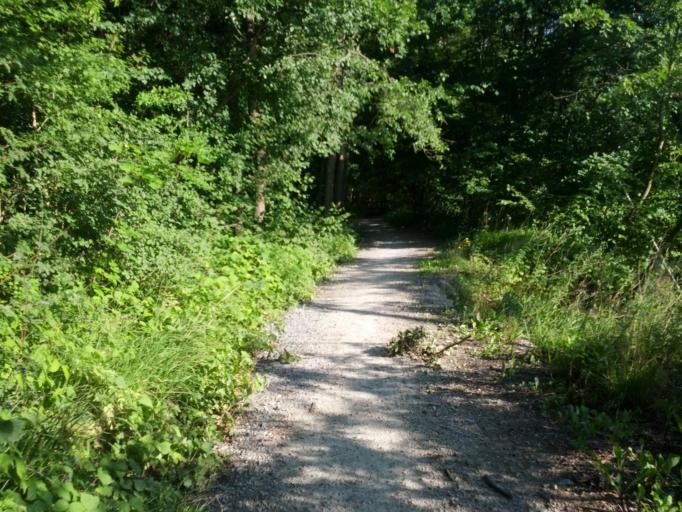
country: DE
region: Thuringia
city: Creuzburg
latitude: 51.0633
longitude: 10.2744
